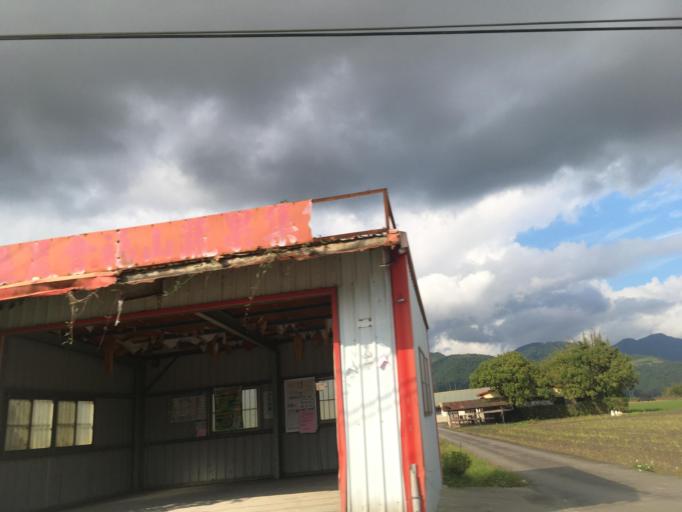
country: TW
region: Taiwan
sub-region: Yilan
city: Yilan
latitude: 24.6669
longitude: 121.6257
